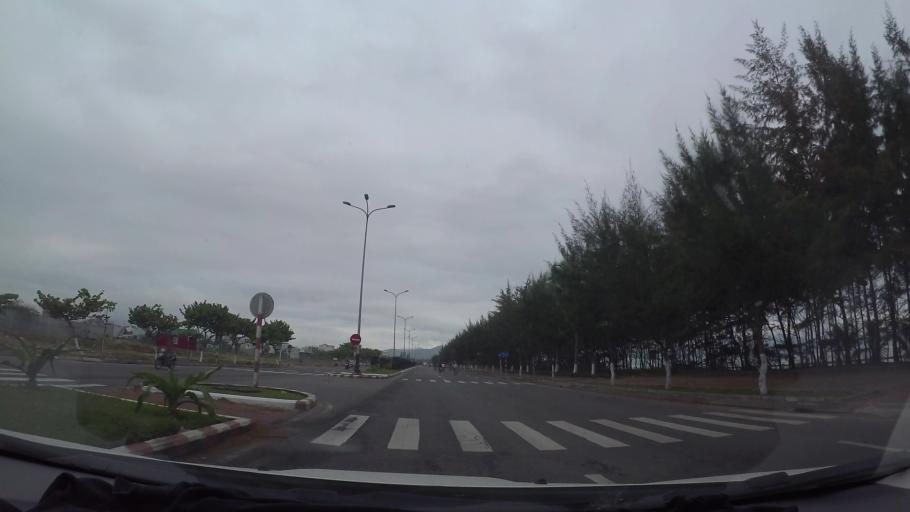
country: VN
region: Da Nang
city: Lien Chieu
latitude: 16.0896
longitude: 108.1531
